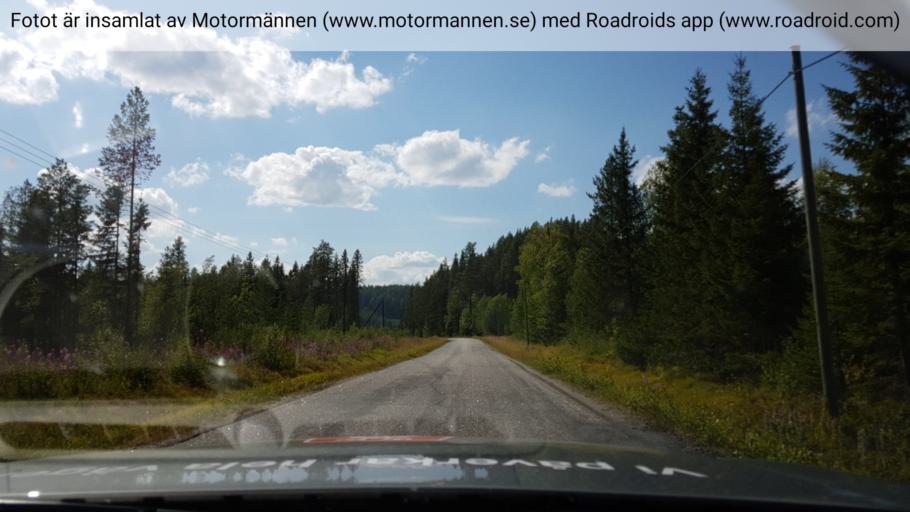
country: SE
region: Vaesterbotten
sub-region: Dorotea Kommun
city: Dorotea
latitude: 64.1271
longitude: 16.2845
